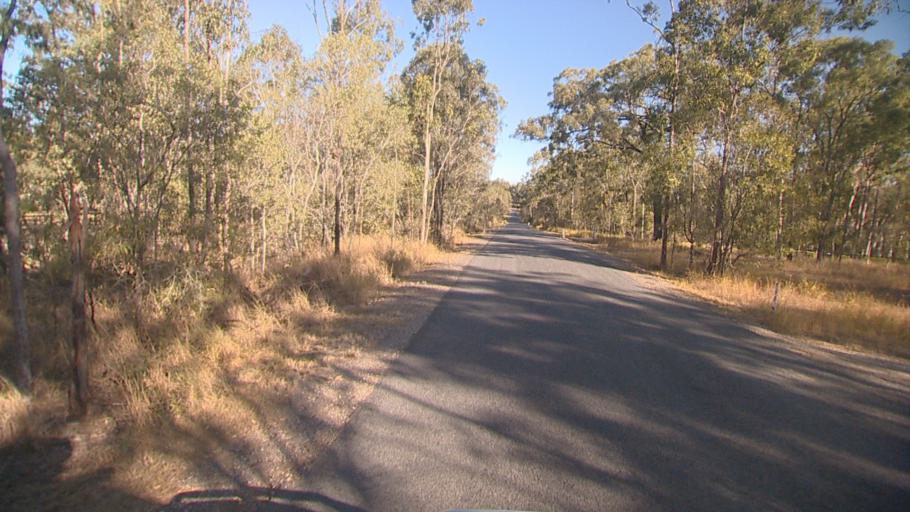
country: AU
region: Queensland
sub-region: Logan
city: North Maclean
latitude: -27.7996
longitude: 153.0256
